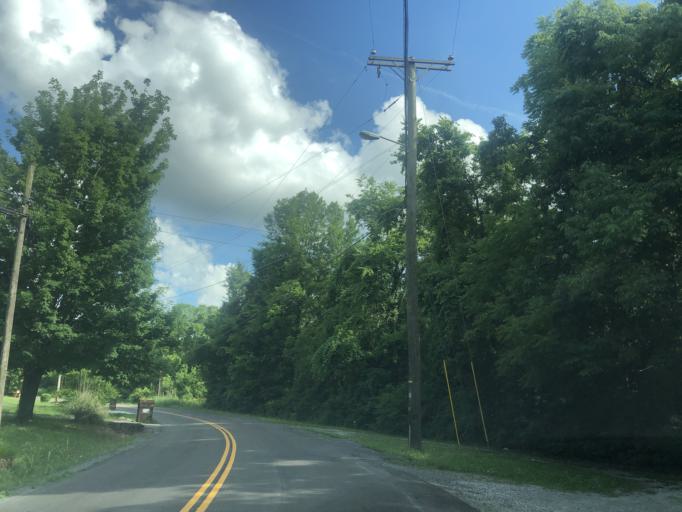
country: US
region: Tennessee
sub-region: Davidson County
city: Nashville
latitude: 36.2228
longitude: -86.8523
